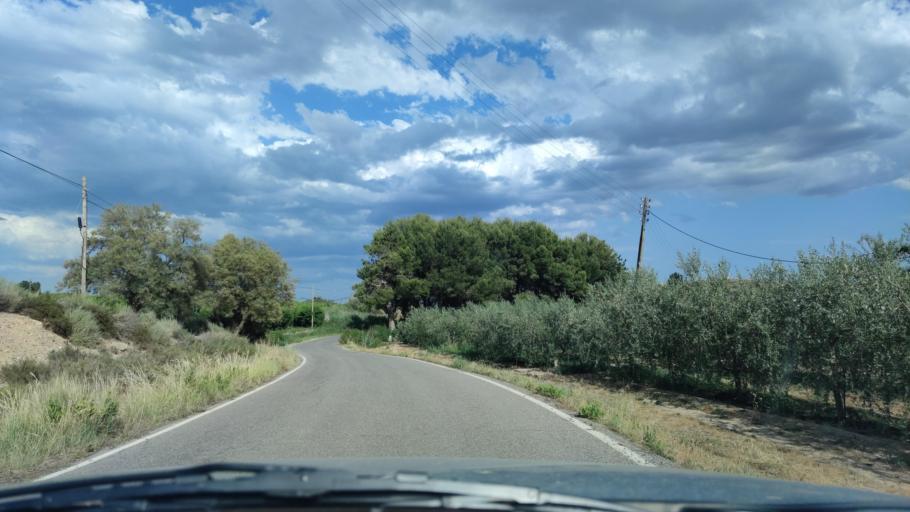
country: ES
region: Catalonia
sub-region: Provincia de Lleida
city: Alpicat
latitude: 41.6290
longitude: 0.5694
